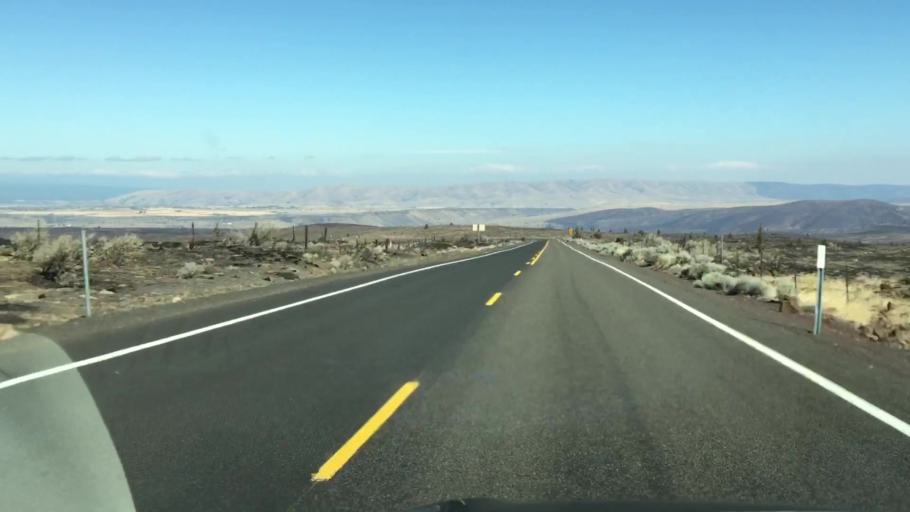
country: US
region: Oregon
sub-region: Jefferson County
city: Warm Springs
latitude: 45.1047
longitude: -121.0397
